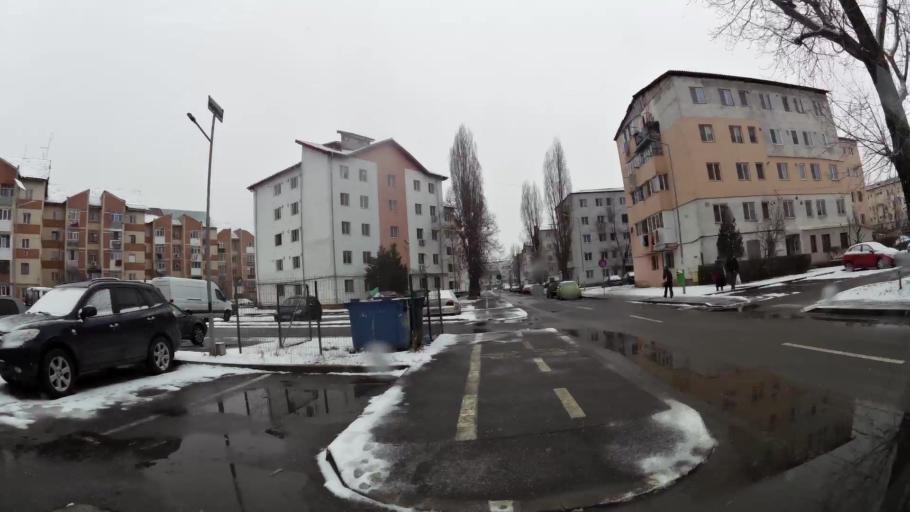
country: RO
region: Dambovita
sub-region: Municipiul Targoviste
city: Targoviste
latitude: 44.9255
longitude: 25.4469
